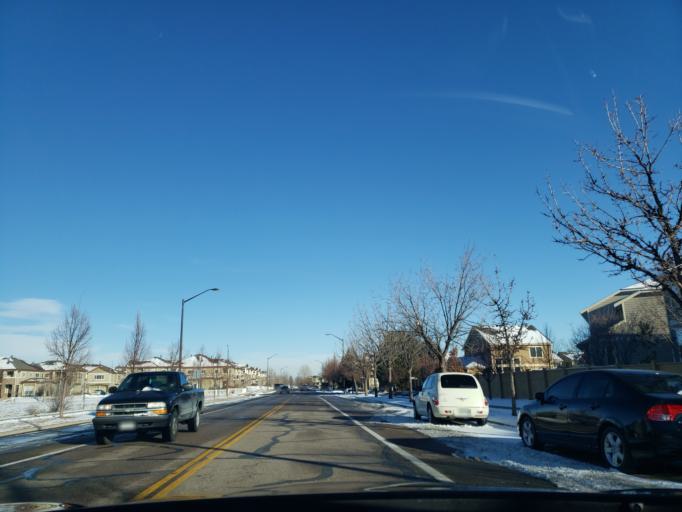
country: US
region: Colorado
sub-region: Larimer County
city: Fort Collins
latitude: 40.5160
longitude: -105.0085
